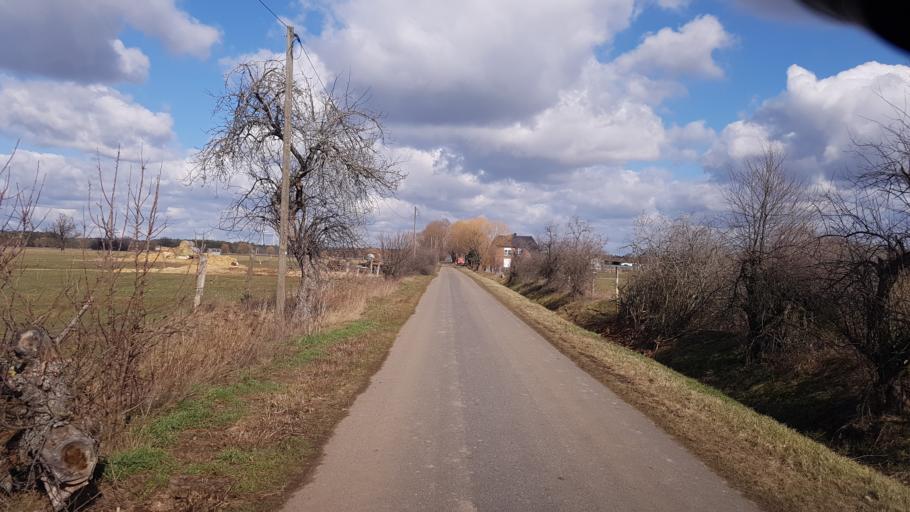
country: DE
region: Brandenburg
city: Falkenberg
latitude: 51.5910
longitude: 13.2148
